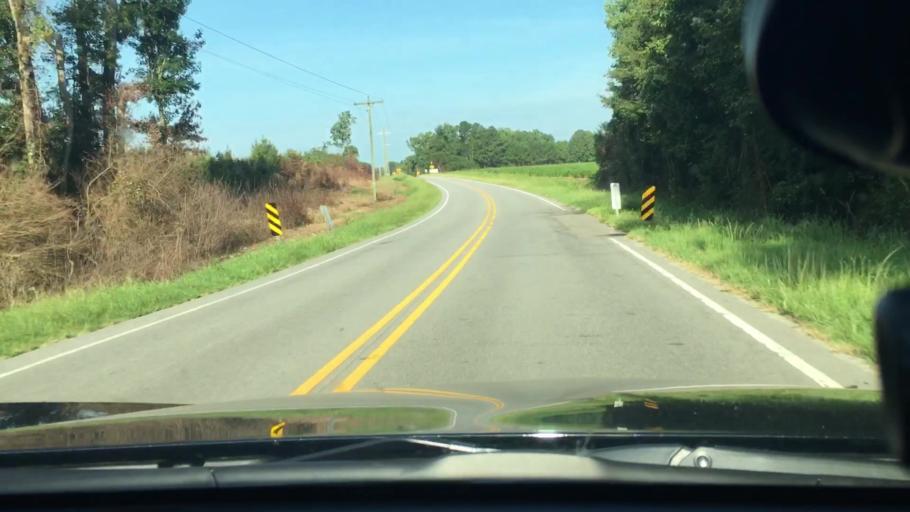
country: US
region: North Carolina
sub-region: Edgecombe County
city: Pinetops
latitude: 35.7803
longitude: -77.5982
